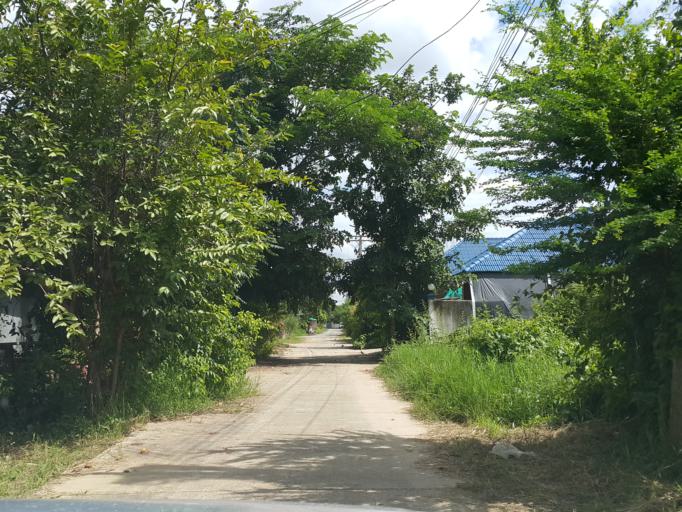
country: TH
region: Chiang Mai
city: San Kamphaeng
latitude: 18.7552
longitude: 99.1247
